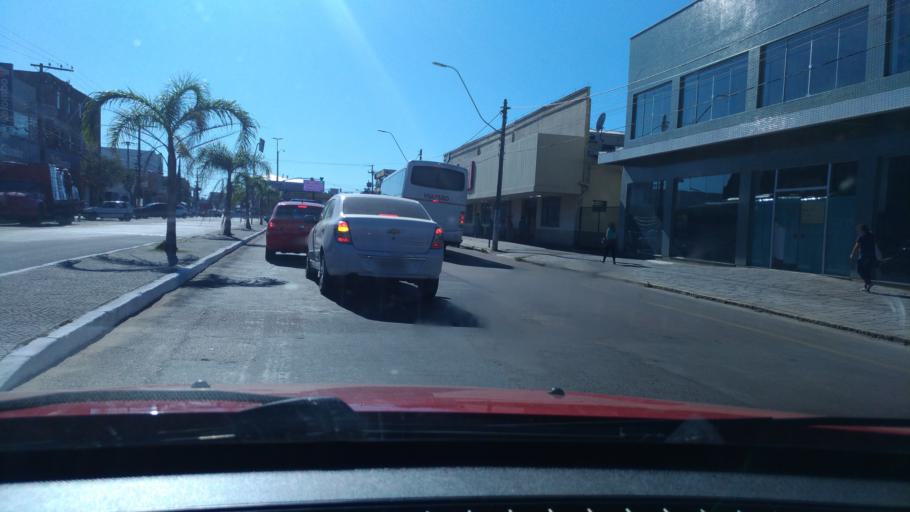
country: BR
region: Rio Grande do Sul
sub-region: Viamao
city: Viamao
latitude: -30.0828
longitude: -51.0309
